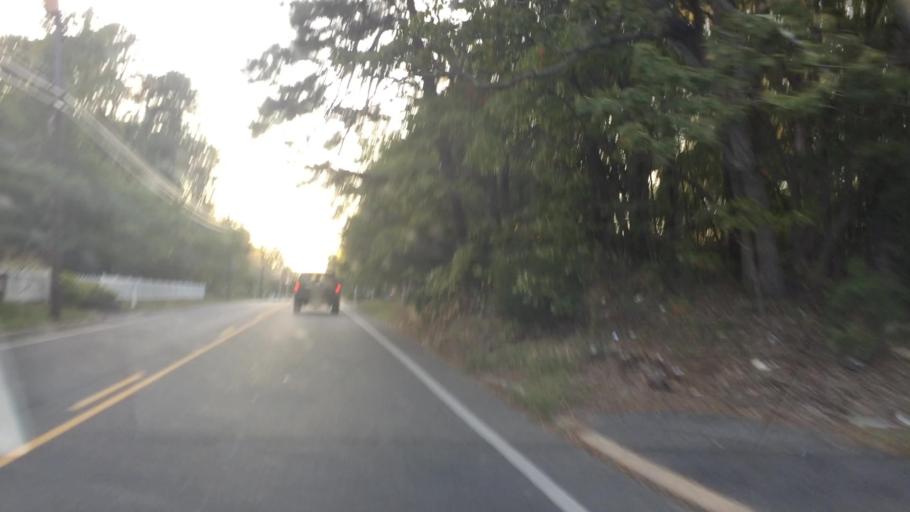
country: US
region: New Jersey
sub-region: Ocean County
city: Barnegat
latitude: 39.7551
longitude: -74.2314
